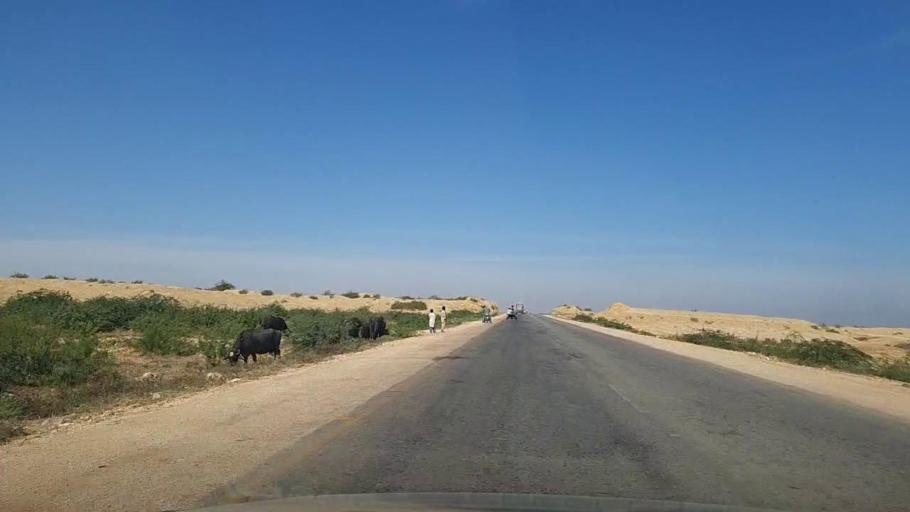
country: PK
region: Sindh
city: Kotri
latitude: 25.2092
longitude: 68.2375
